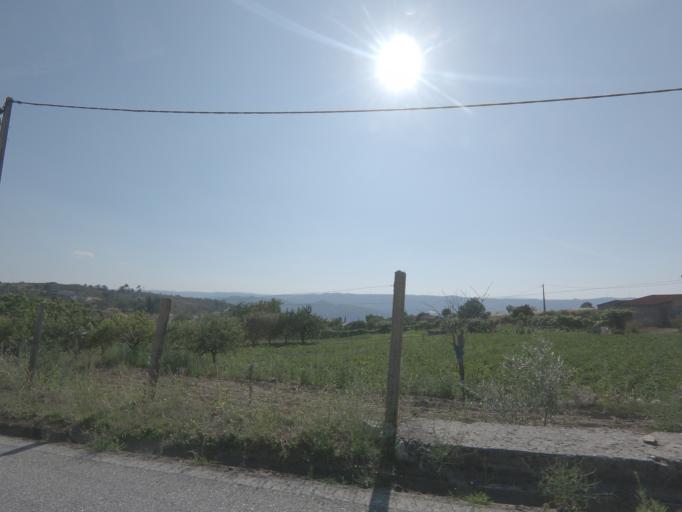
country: PT
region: Viseu
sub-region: Tabuaco
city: Tabuaco
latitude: 41.0501
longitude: -7.5671
